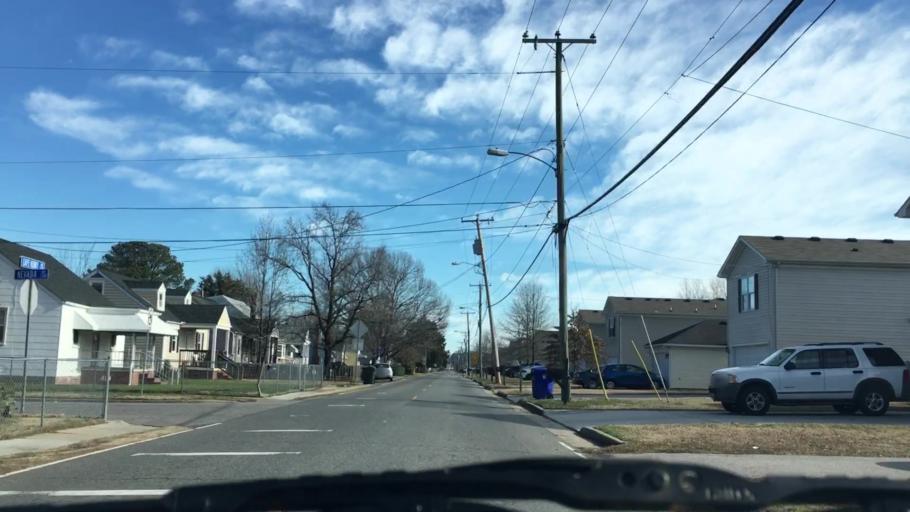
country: US
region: Virginia
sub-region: City of Norfolk
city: Norfolk
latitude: 36.8660
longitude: -76.2430
